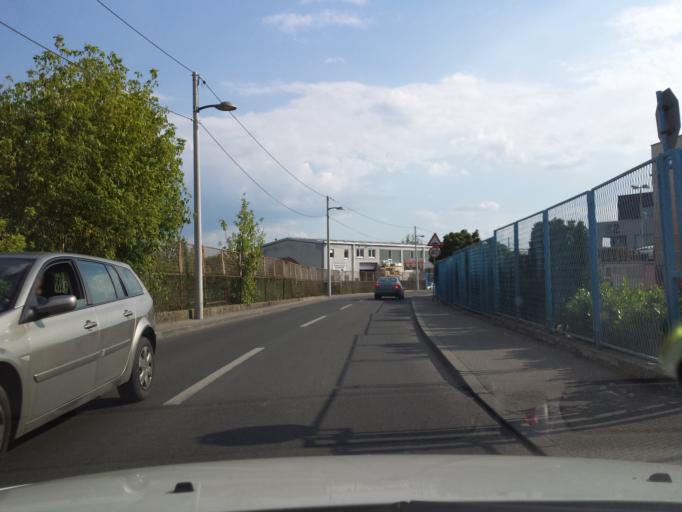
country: HR
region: Grad Zagreb
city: Jankomir
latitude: 45.8051
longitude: 15.9242
